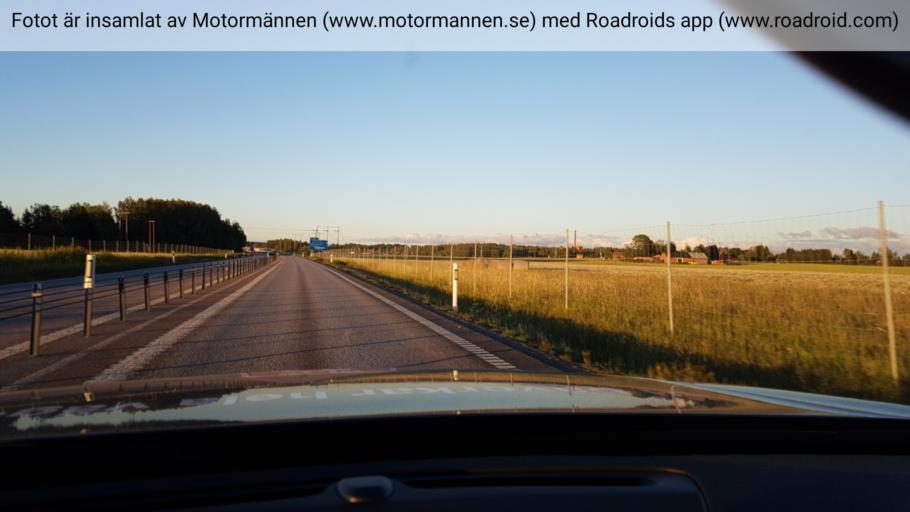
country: SE
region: Vaestmanland
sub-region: Hallstahammars Kommun
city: Hallstahammar
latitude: 59.5849
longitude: 16.1914
